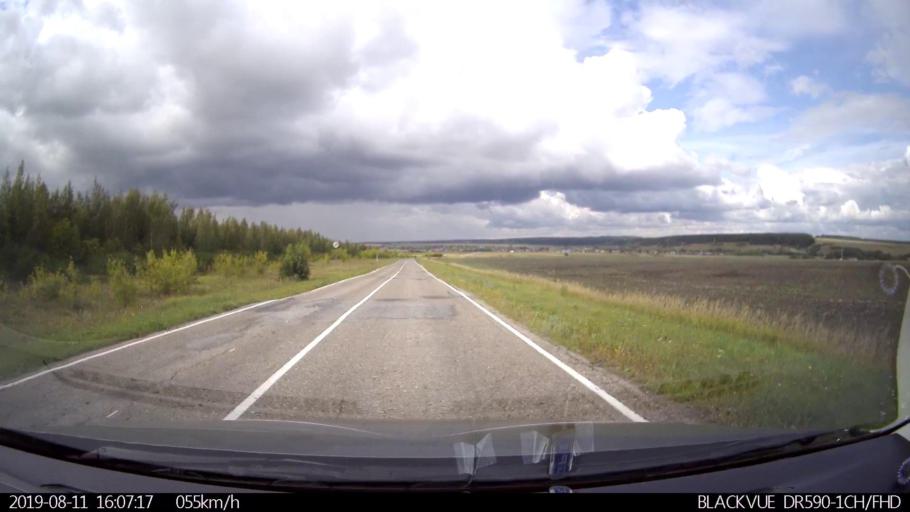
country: RU
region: Ulyanovsk
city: Ignatovka
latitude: 53.9749
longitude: 47.6495
